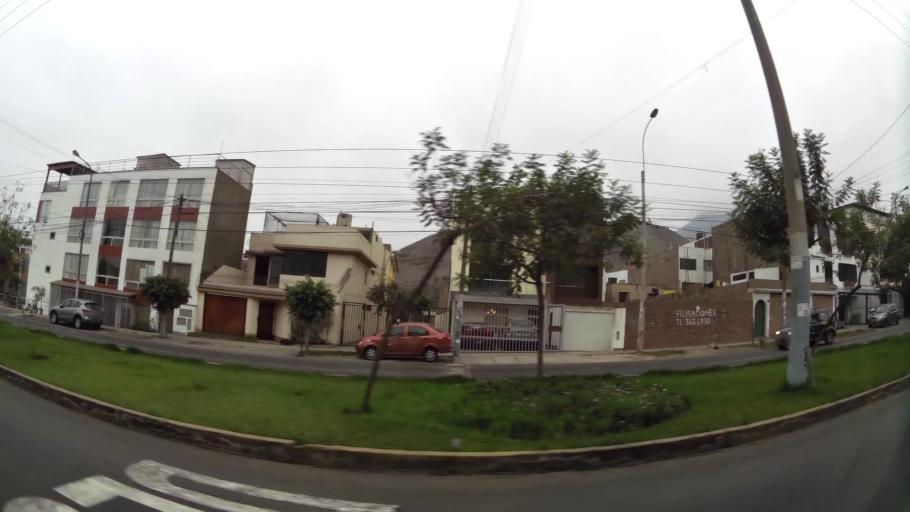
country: PE
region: Lima
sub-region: Lima
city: La Molina
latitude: -12.1060
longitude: -76.9406
